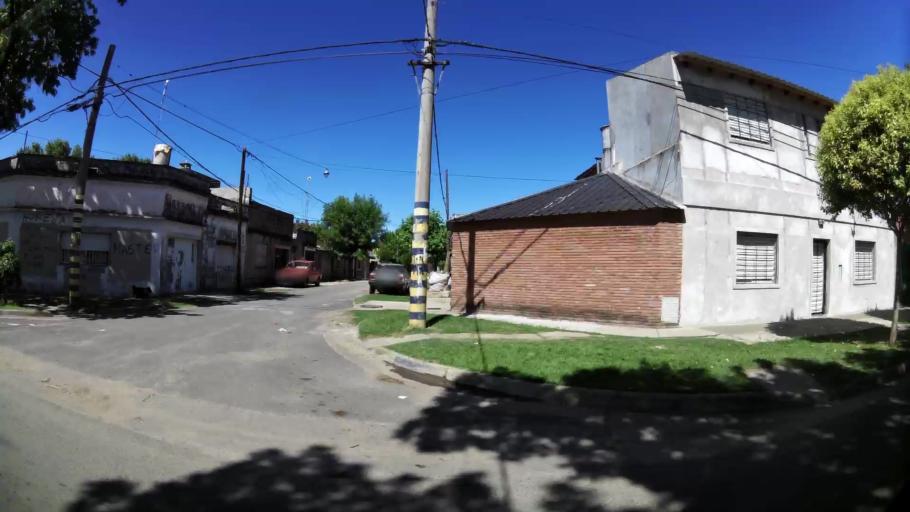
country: AR
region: Santa Fe
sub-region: Departamento de Rosario
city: Rosario
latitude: -32.9336
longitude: -60.6949
